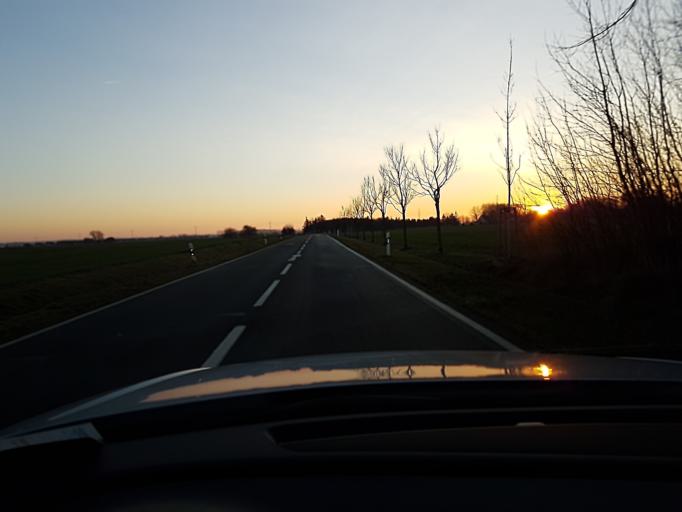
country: DE
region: Mecklenburg-Vorpommern
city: Wiek
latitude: 54.5730
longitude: 13.2651
